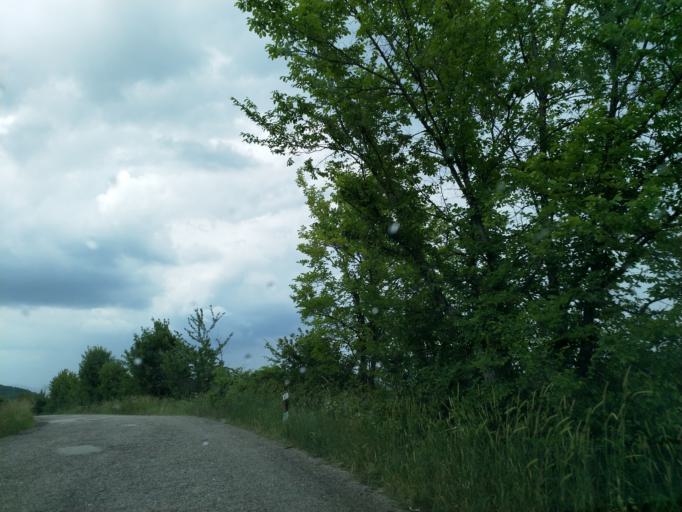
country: RS
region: Central Serbia
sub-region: Zajecarski Okrug
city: Boljevac
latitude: 43.9776
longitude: 21.9733
